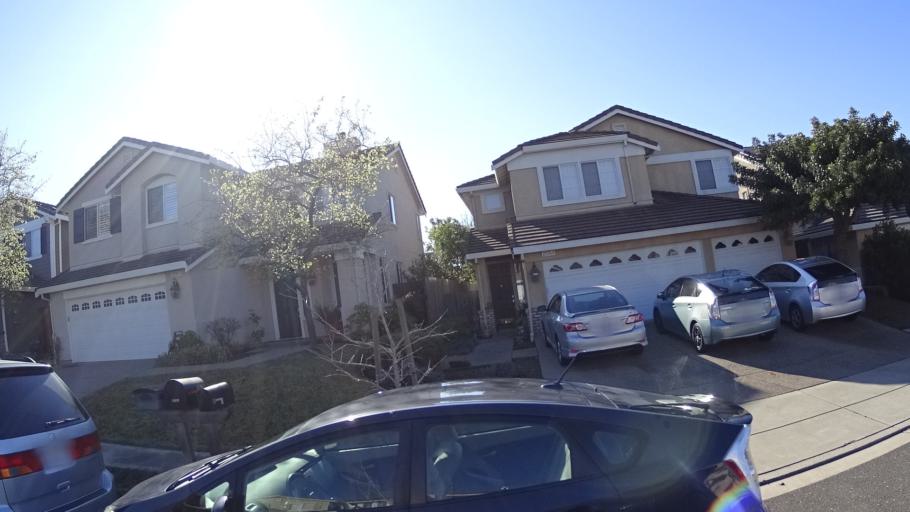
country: US
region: California
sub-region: Alameda County
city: Fairview
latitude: 37.6801
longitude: -122.0337
